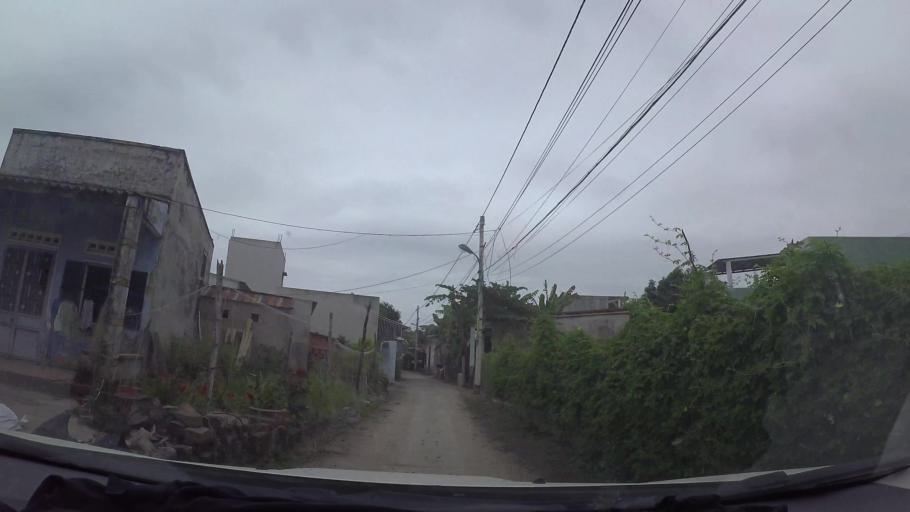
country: VN
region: Da Nang
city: Lien Chieu
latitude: 16.1034
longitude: 108.1305
